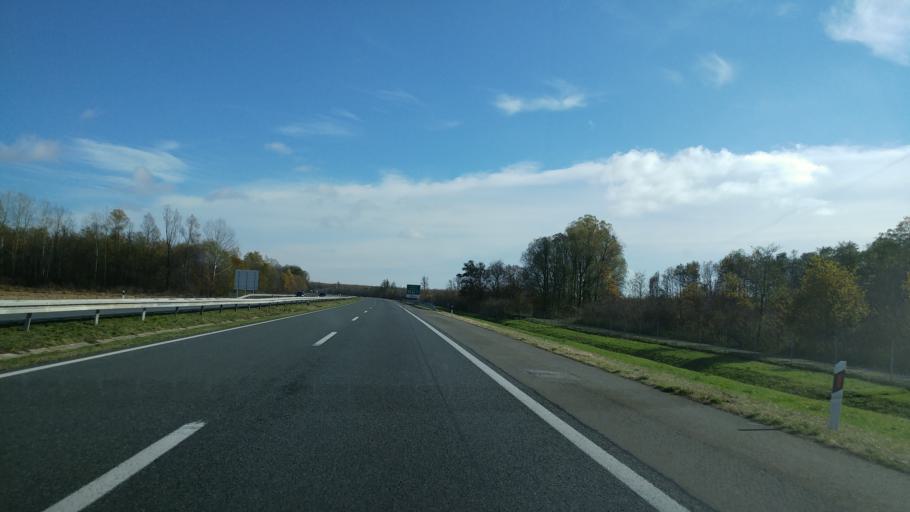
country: HR
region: Sisacko-Moslavacka
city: Novska
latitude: 45.3167
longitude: 16.9795
